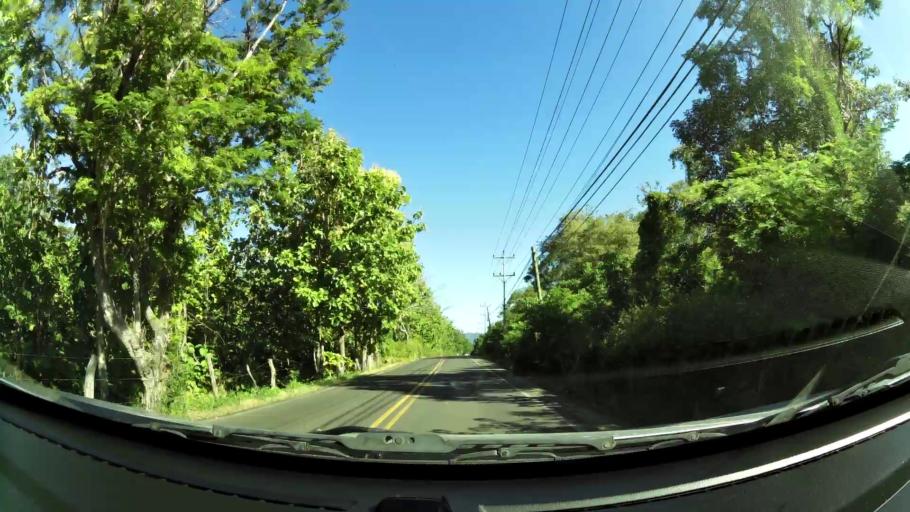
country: CR
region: Guanacaste
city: Sardinal
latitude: 10.4223
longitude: -85.7845
